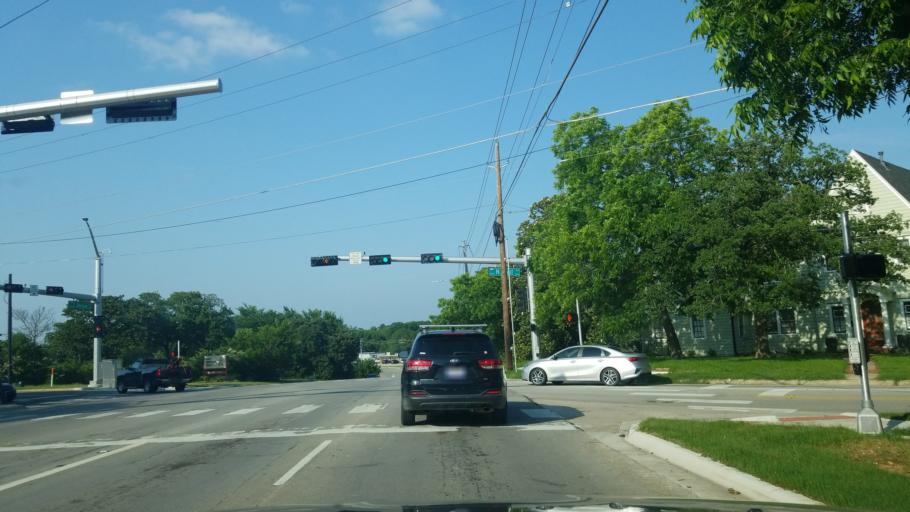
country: US
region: Texas
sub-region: Denton County
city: Denton
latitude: 33.2339
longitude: -97.1274
